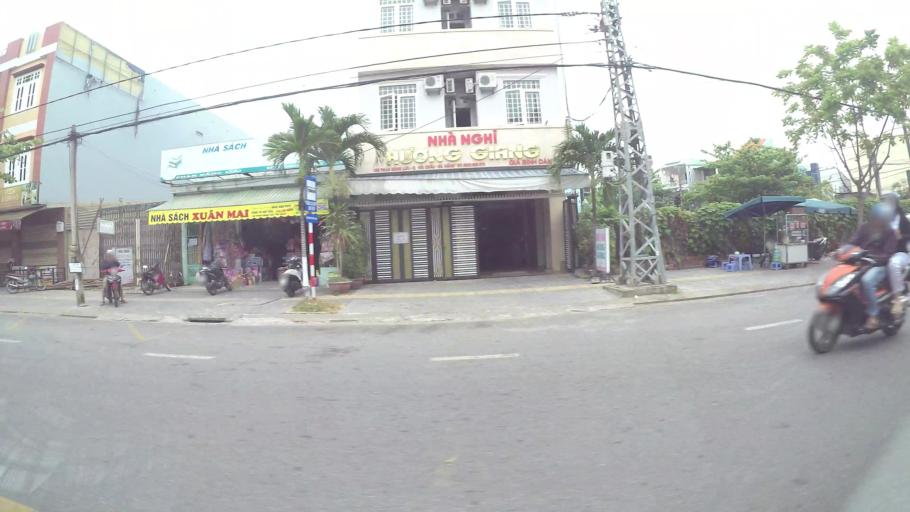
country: VN
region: Da Nang
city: Cam Le
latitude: 16.0362
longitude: 108.2168
